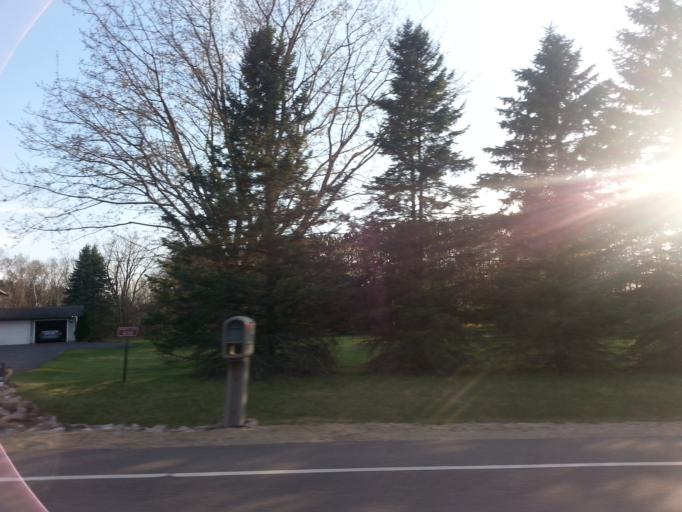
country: US
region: Minnesota
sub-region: Washington County
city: Lake Saint Croix Beach
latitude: 44.9252
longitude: -92.6949
